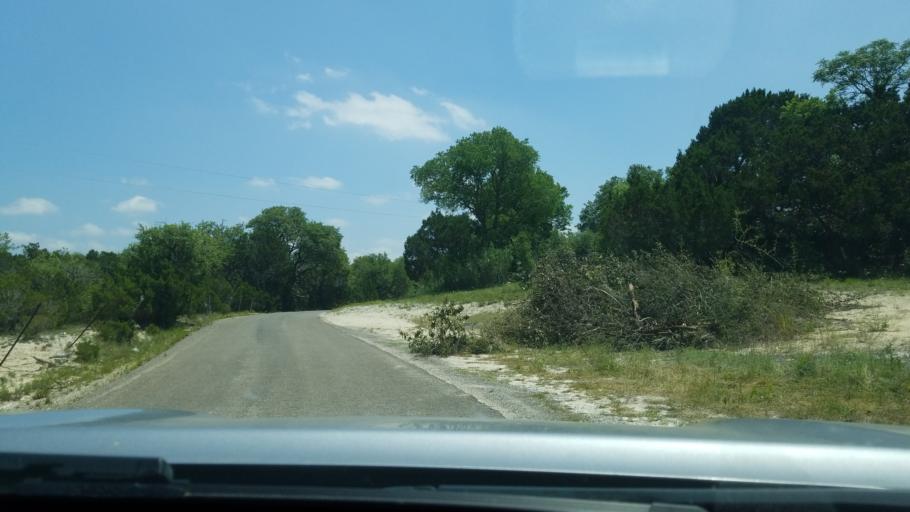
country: US
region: Texas
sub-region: Blanco County
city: Blanco
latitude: 30.0814
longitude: -98.4012
